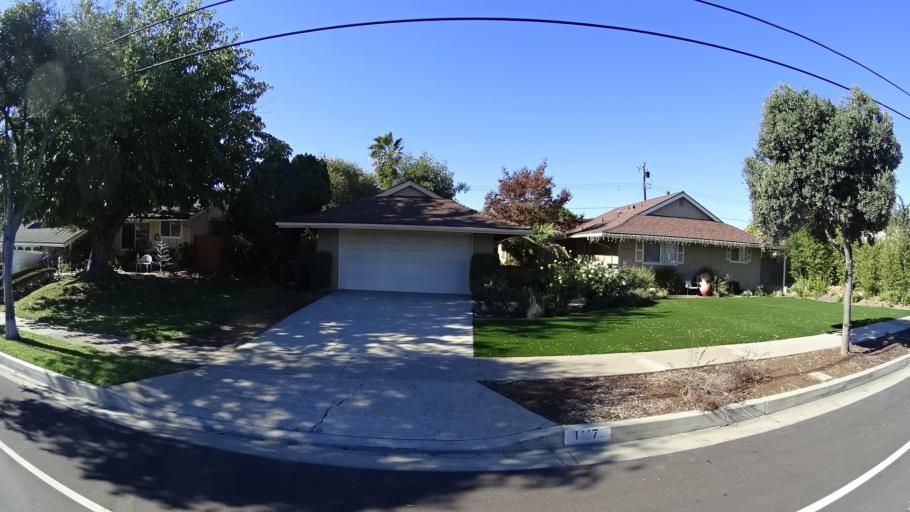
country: US
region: California
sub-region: Orange County
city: Brea
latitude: 33.9364
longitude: -117.9157
